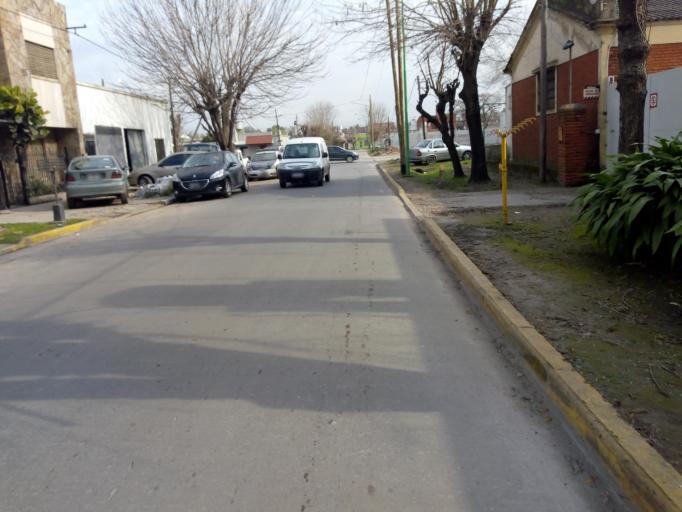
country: AR
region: Buenos Aires
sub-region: Partido de La Plata
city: La Plata
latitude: -34.8954
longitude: -57.9362
